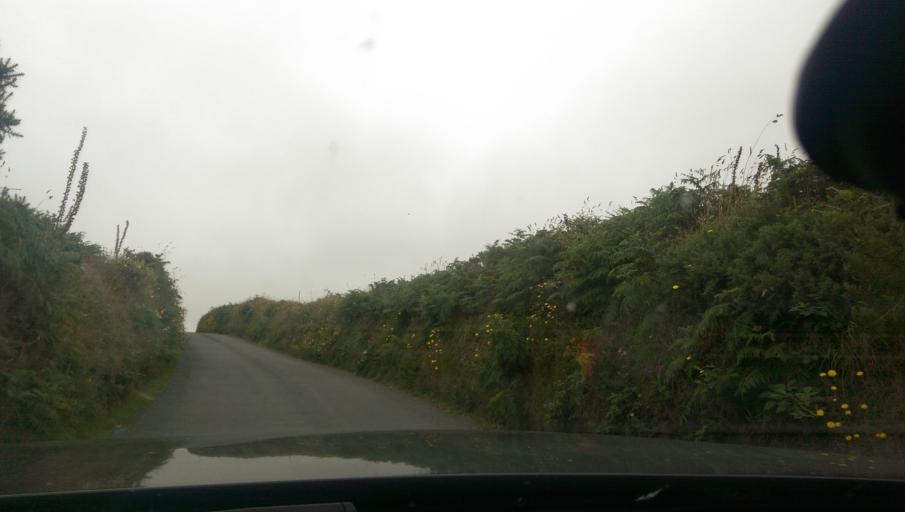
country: GB
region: England
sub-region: Cornwall
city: St. Buryan
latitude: 50.0970
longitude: -5.6507
